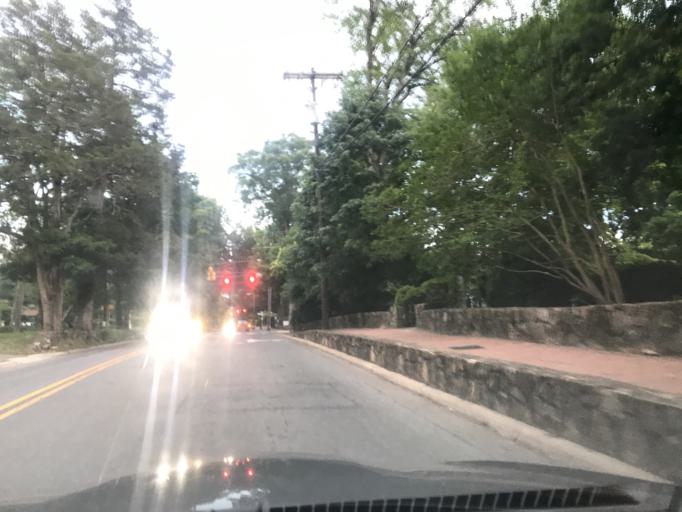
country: US
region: North Carolina
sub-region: Orange County
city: Chapel Hill
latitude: 35.9171
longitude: -79.0501
